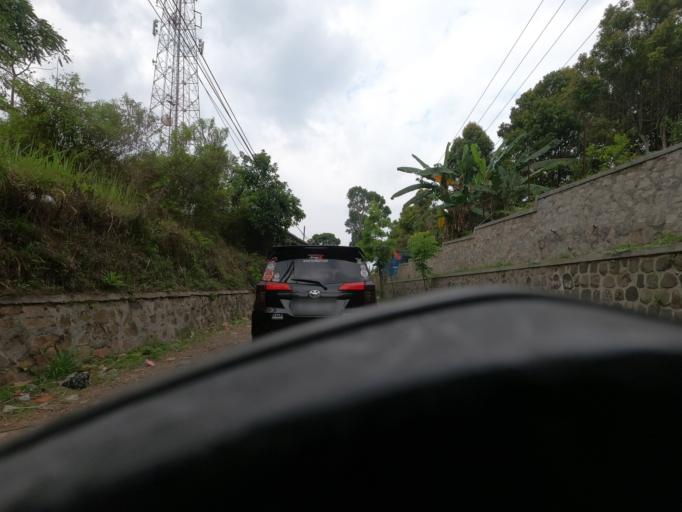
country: ID
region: West Java
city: Cimahi
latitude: -6.8148
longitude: 107.5577
